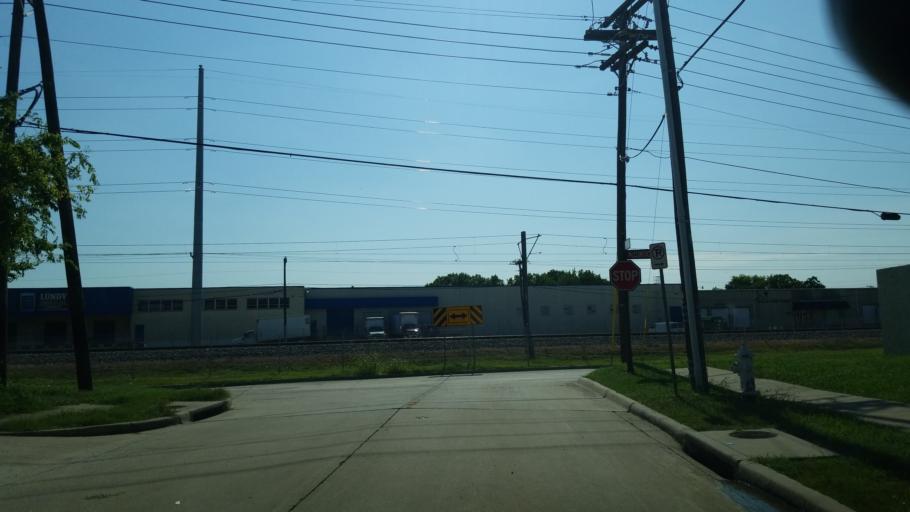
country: US
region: Texas
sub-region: Dallas County
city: Farmers Branch
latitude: 32.9293
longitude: -96.8980
